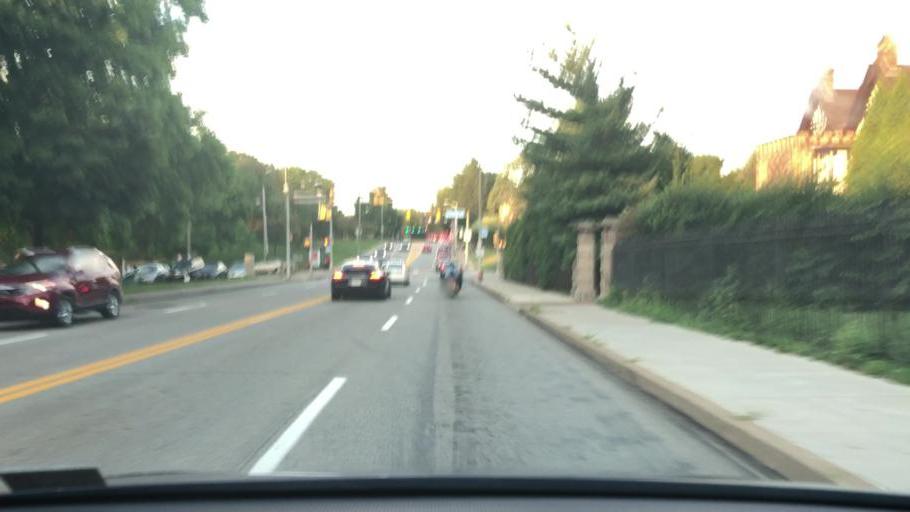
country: US
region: Pennsylvania
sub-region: Allegheny County
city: Bloomfield
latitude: 40.4534
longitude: -79.9162
